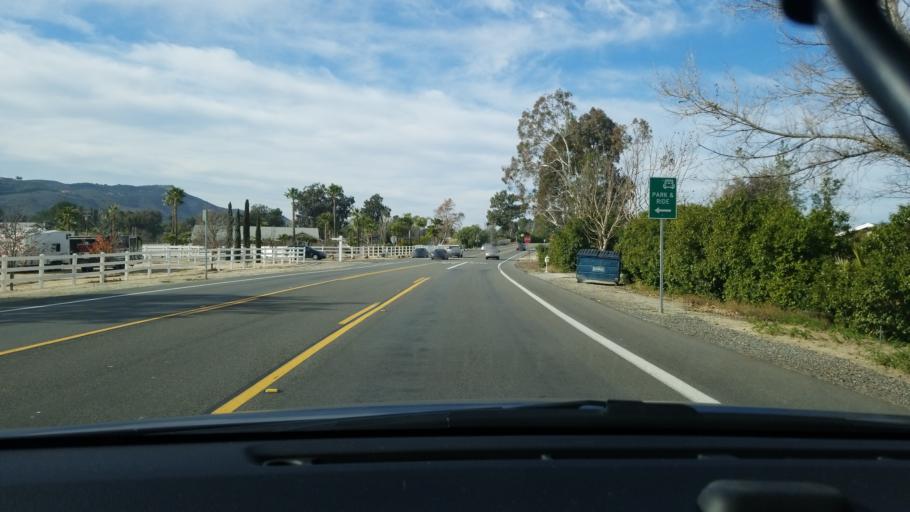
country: US
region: California
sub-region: Riverside County
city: Temecula
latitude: 33.4809
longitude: -117.1317
